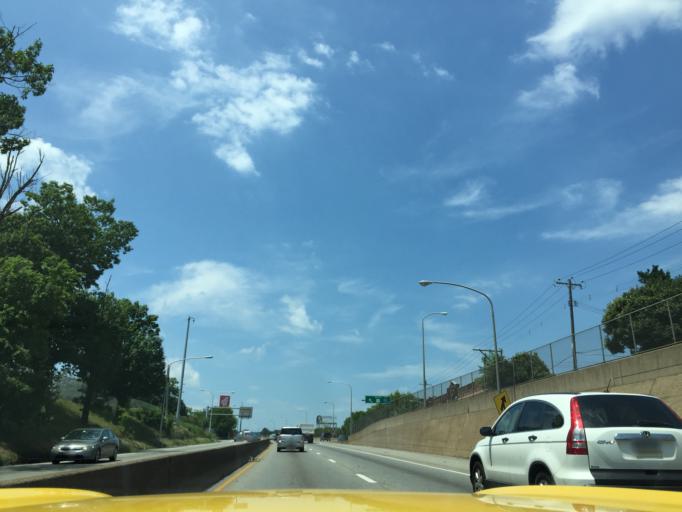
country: US
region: Pennsylvania
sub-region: Philadelphia County
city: Philadelphia
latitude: 40.0203
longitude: -75.1526
